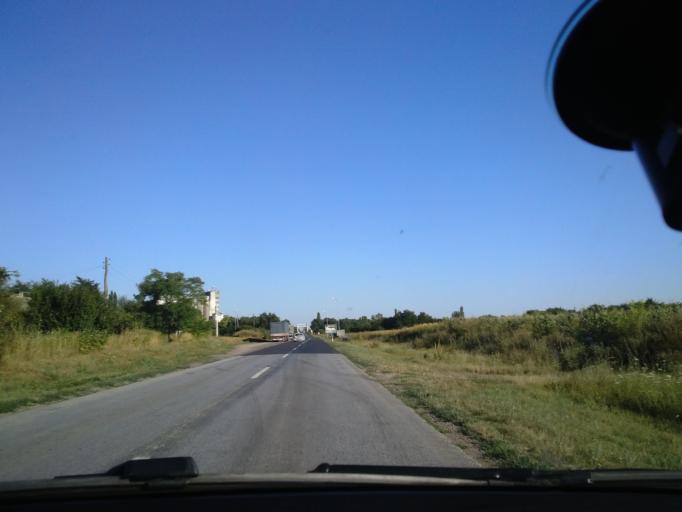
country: RS
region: Autonomna Pokrajina Vojvodina
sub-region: Zapadnobacki Okrug
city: Sombor
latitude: 45.7405
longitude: 19.1363
